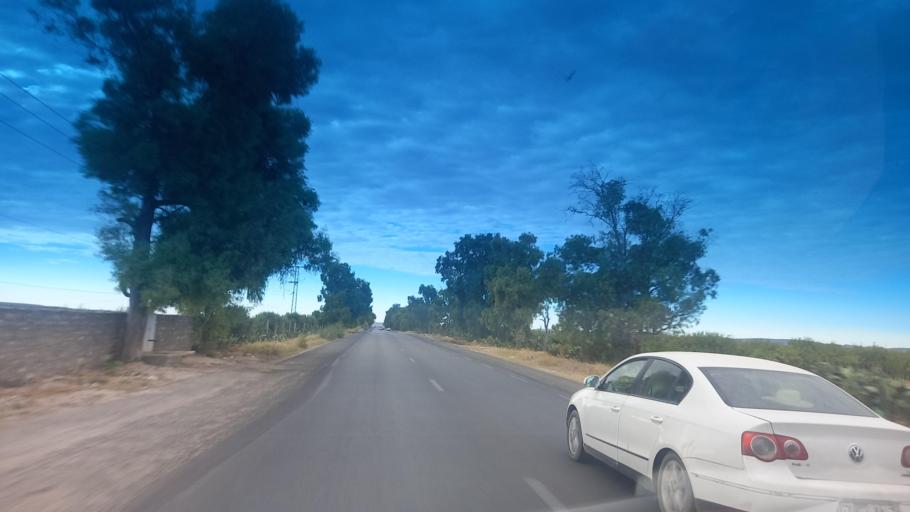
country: TN
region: Al Qasrayn
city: Sbiba
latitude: 35.2937
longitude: 9.0905
